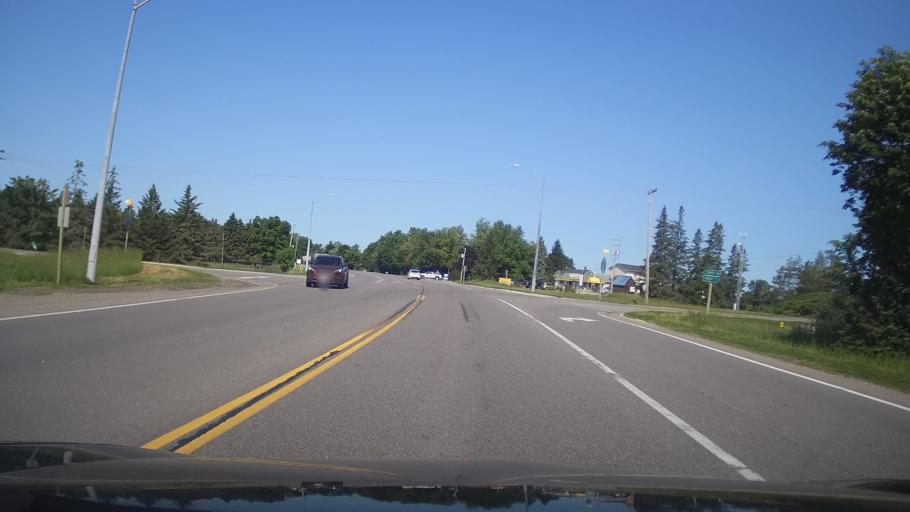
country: CA
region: Ontario
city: Omemee
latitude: 44.3479
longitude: -78.8034
